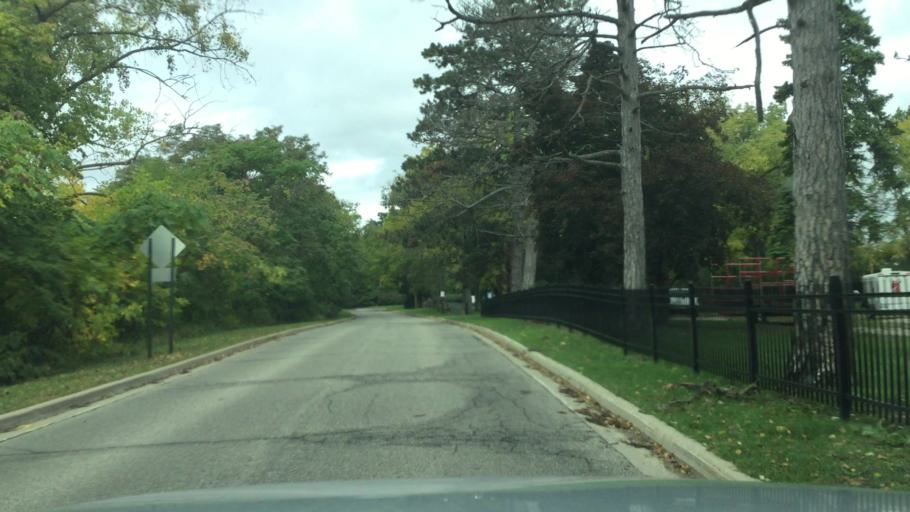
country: US
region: Michigan
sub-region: Oakland County
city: Orchard Lake
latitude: 42.5943
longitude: -83.3594
